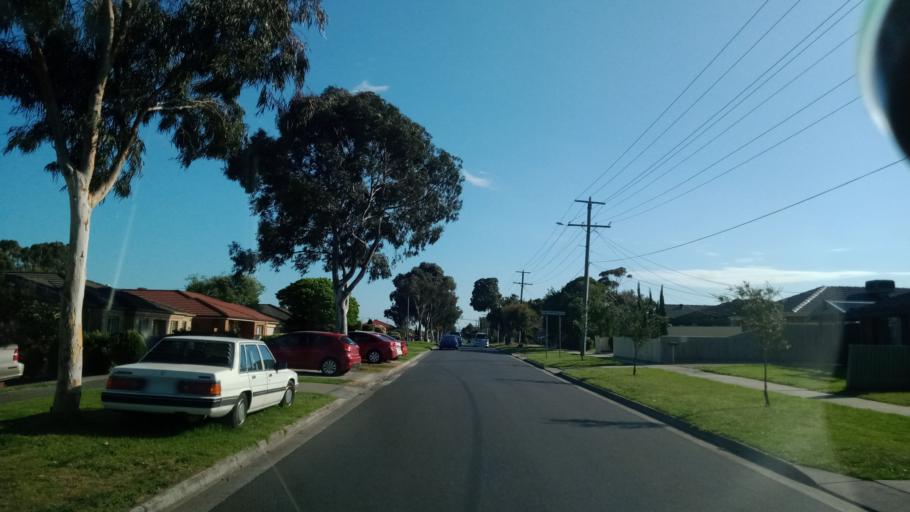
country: AU
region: Victoria
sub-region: Casey
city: Cranbourne West
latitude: -38.0957
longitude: 145.2680
